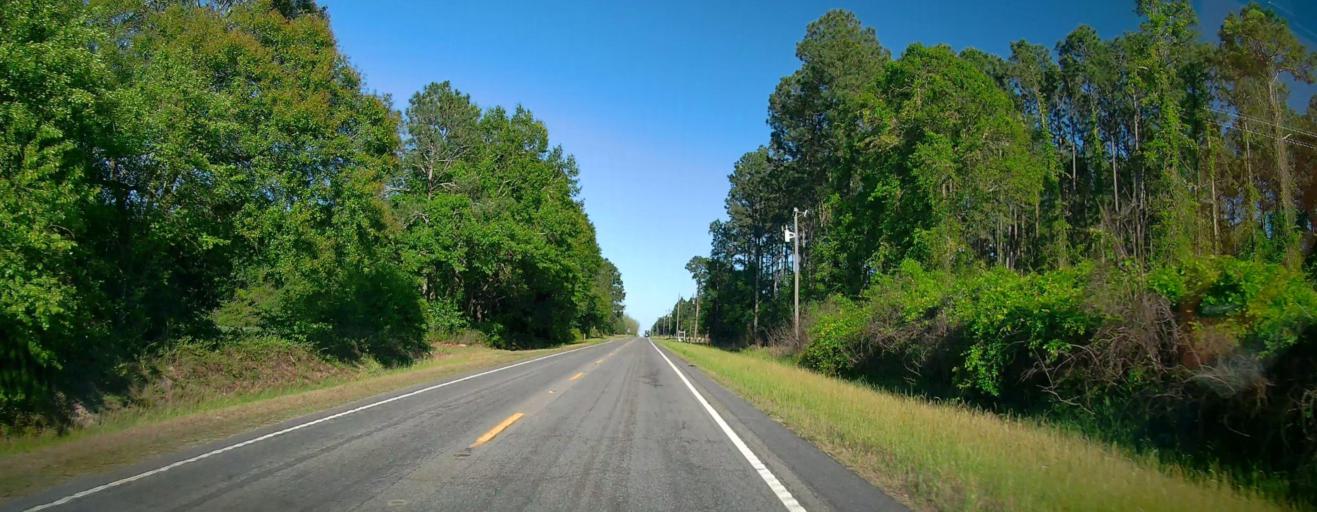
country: US
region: Georgia
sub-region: Ben Hill County
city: Fitzgerald
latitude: 31.7186
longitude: -83.3422
